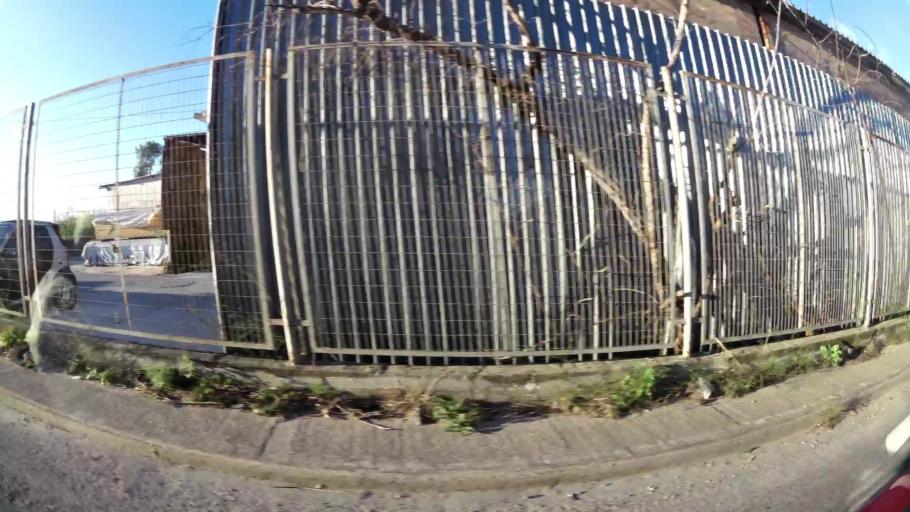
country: GR
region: Attica
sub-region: Nomarchia Anatolikis Attikis
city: Pallini
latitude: 37.9983
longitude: 23.8656
